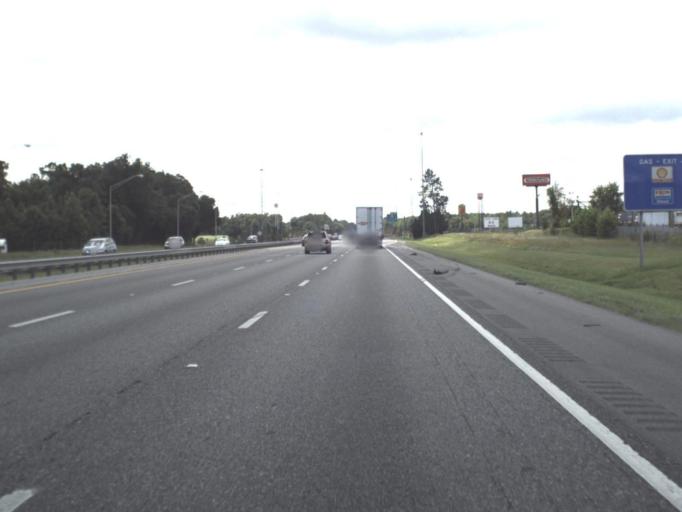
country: US
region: Florida
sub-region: Columbia County
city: Lake City
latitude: 30.1228
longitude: -82.6589
